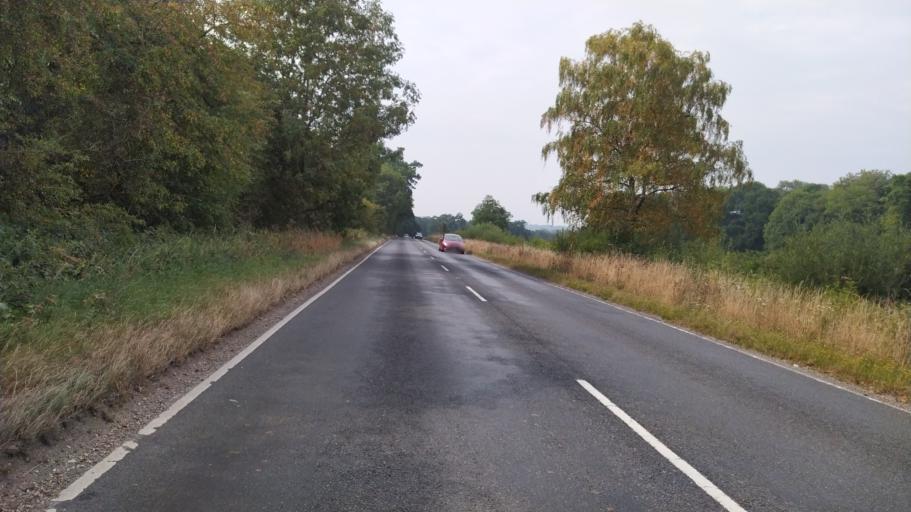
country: GB
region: England
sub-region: Hampshire
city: Romsey
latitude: 50.9800
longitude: -1.4726
